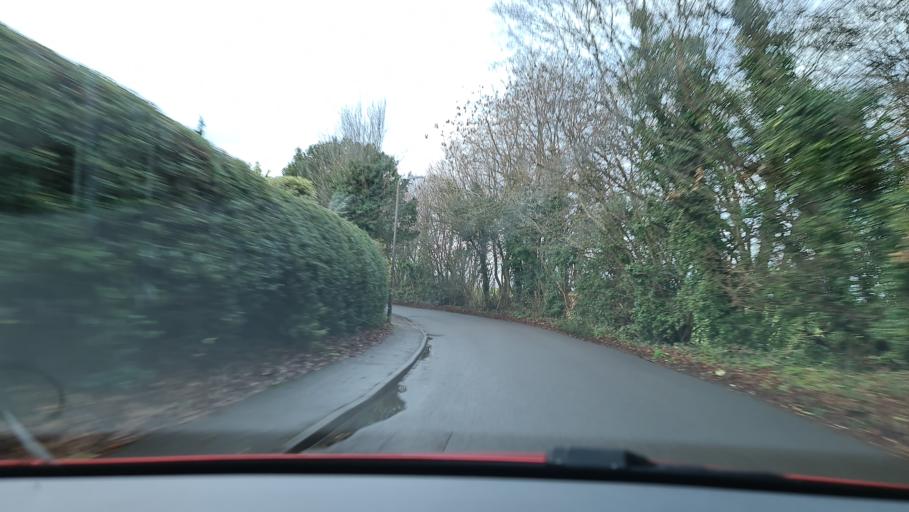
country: GB
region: England
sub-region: Buckinghamshire
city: Little Chalfont
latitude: 51.6745
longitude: -0.5667
